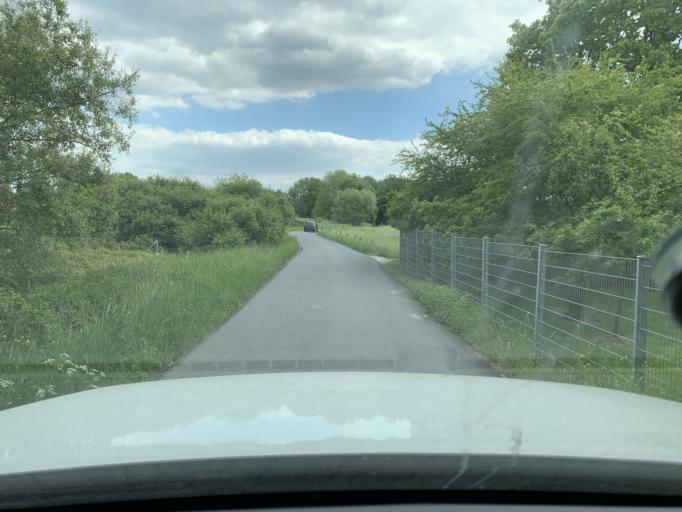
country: DE
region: North Rhine-Westphalia
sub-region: Regierungsbezirk Dusseldorf
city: Muelheim (Ruhr)
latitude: 51.3822
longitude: 6.8740
